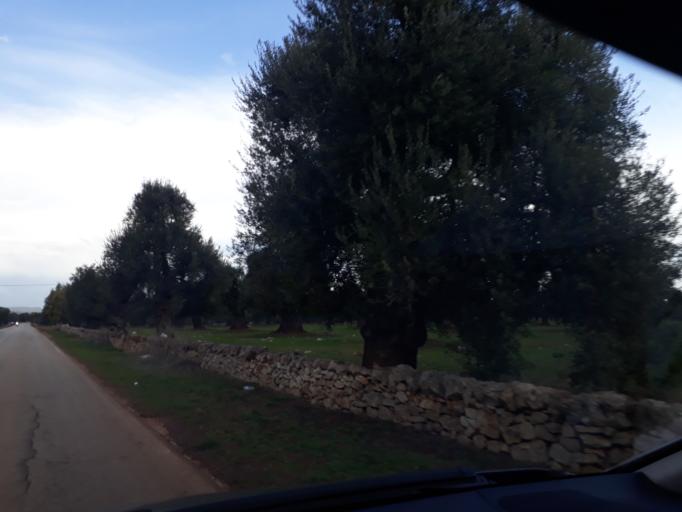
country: IT
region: Apulia
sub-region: Provincia di Brindisi
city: Pezze di Greco
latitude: 40.8093
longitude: 17.3872
